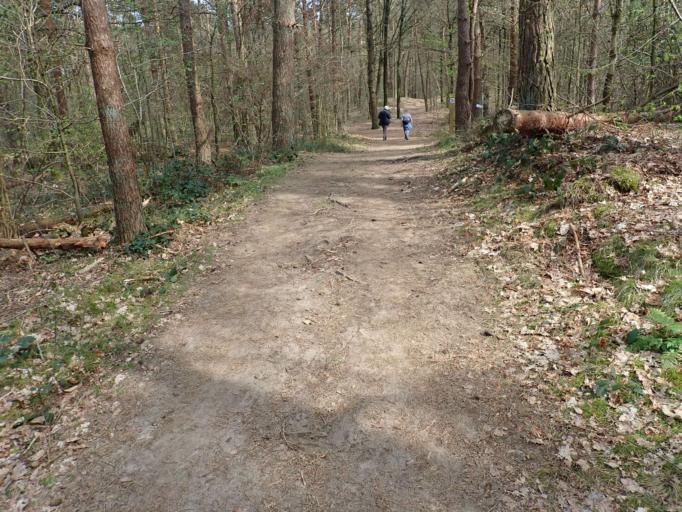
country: BE
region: Flanders
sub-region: Provincie Antwerpen
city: Kasterlee
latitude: 51.2338
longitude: 4.9481
